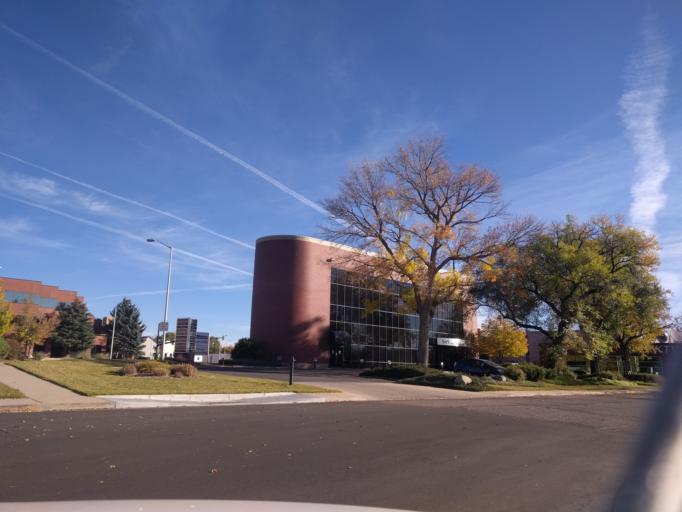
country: US
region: Colorado
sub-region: El Paso County
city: Colorado Springs
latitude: 38.8322
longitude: -104.8162
